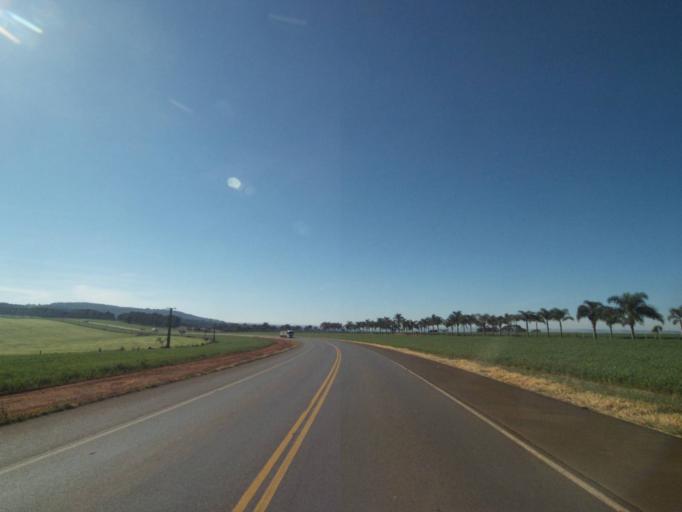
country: BR
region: Parana
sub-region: Tibagi
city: Tibagi
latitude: -24.4235
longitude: -50.3780
